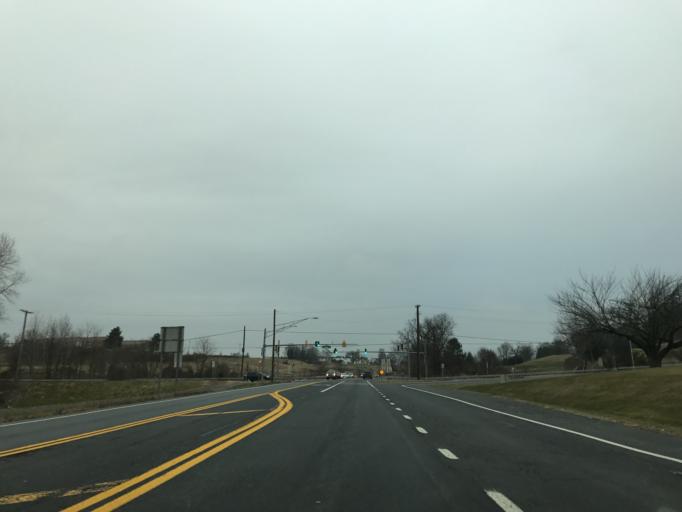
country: US
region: Maryland
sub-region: Carroll County
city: Westminster
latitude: 39.5834
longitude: -77.0091
